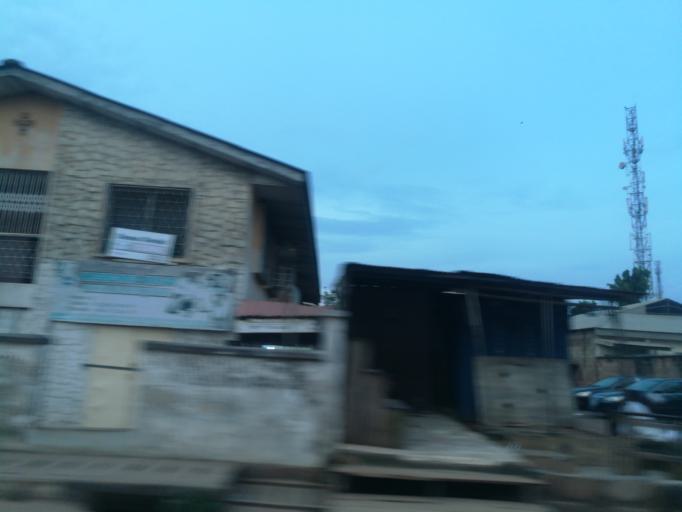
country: NG
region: Oyo
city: Ibadan
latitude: 7.3946
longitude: 3.9053
